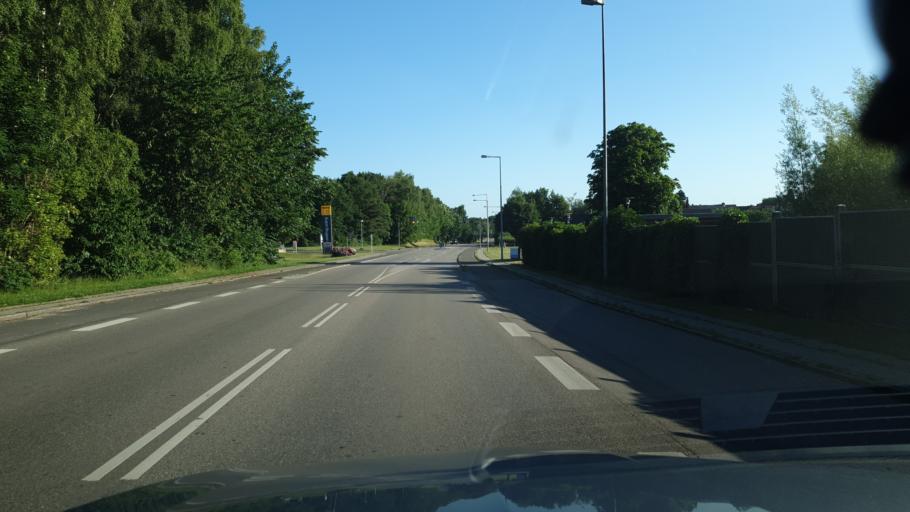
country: DK
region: Zealand
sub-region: Soro Kommune
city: Frederiksberg
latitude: 55.4148
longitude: 11.5649
